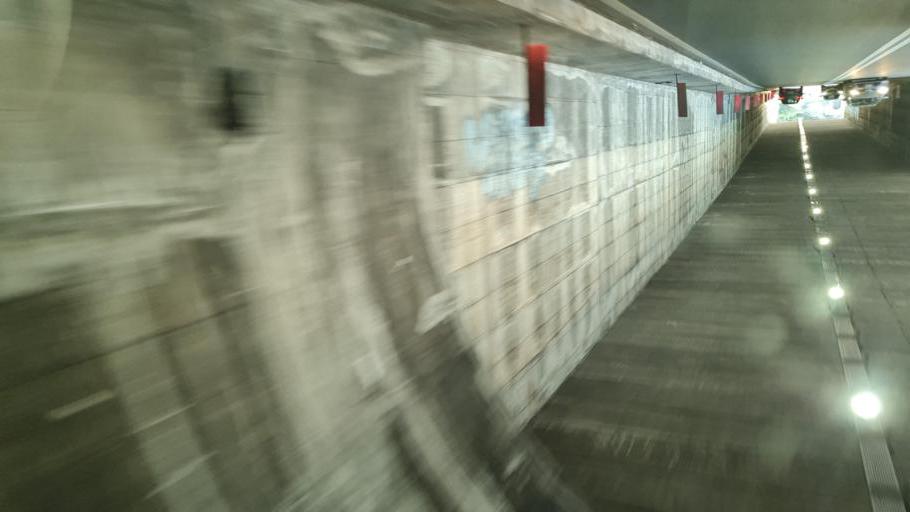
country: IT
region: Liguria
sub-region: Provincia di Savona
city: Noli
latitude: 44.1899
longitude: 8.4140
